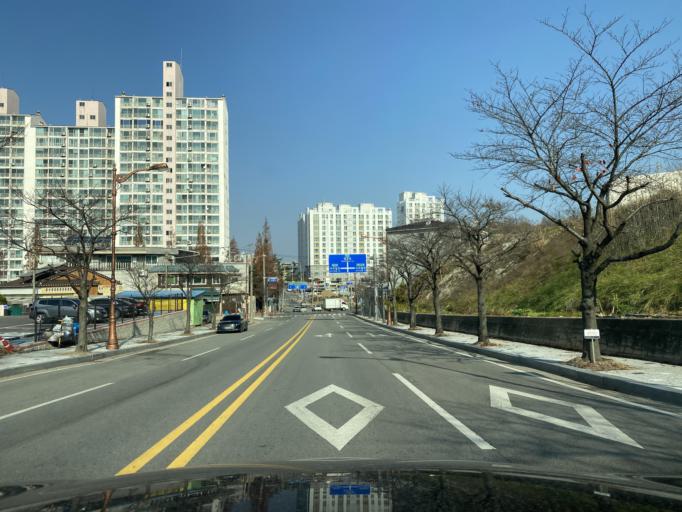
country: KR
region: Chungcheongnam-do
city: Yesan
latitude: 36.6855
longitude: 126.8361
